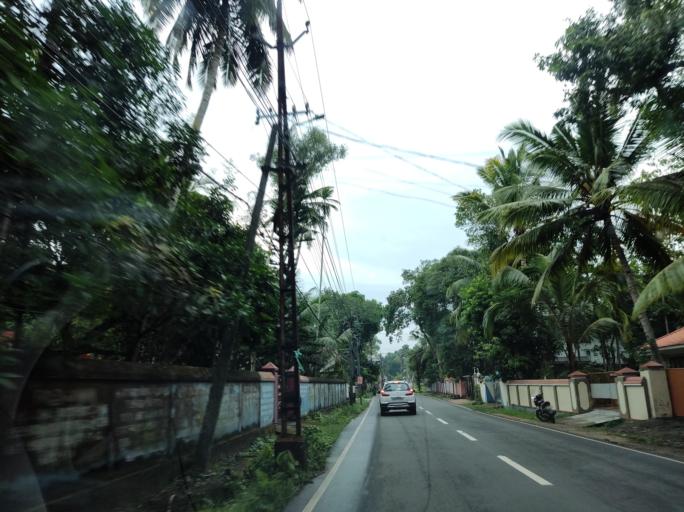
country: IN
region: Kerala
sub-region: Alappuzha
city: Mavelikara
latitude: 9.2520
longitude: 76.5110
